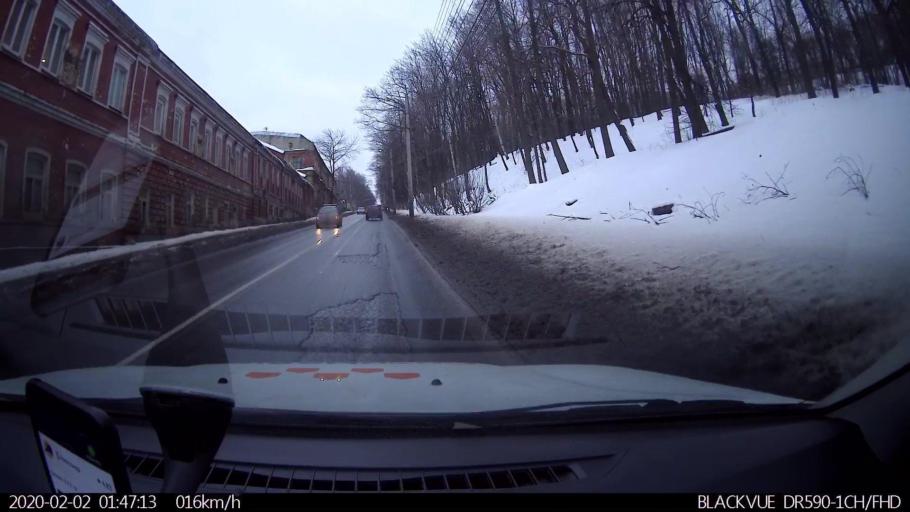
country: RU
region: Nizjnij Novgorod
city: Nizhniy Novgorod
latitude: 56.3339
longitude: 44.0275
